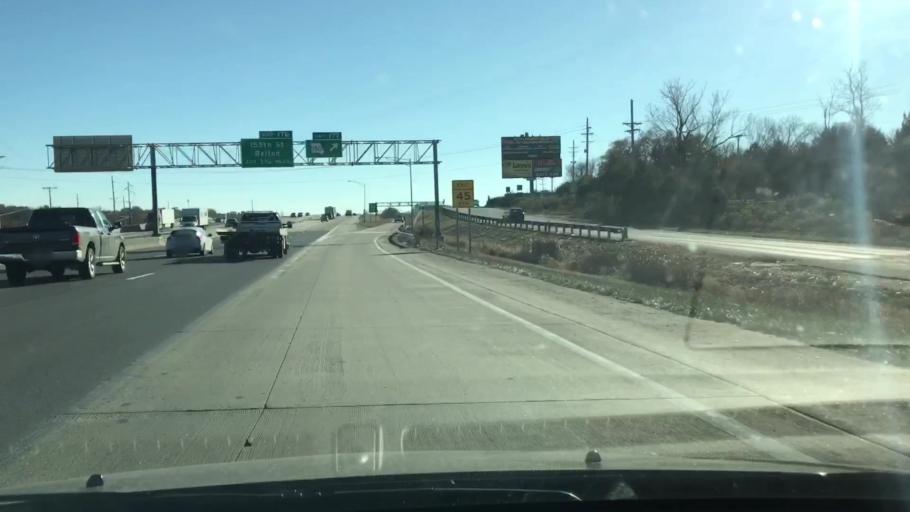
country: US
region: Missouri
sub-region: Jackson County
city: Grandview
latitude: 38.8623
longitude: -94.5273
